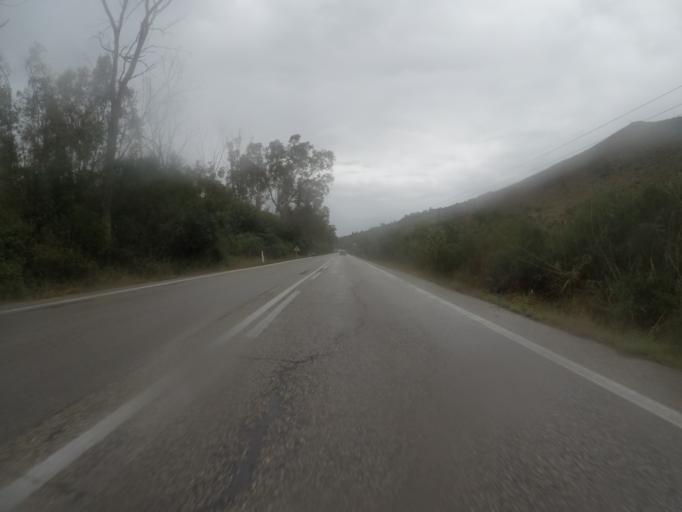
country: GR
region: West Greece
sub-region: Nomos Ileias
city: Zacharo
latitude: 37.5233
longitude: 21.5923
